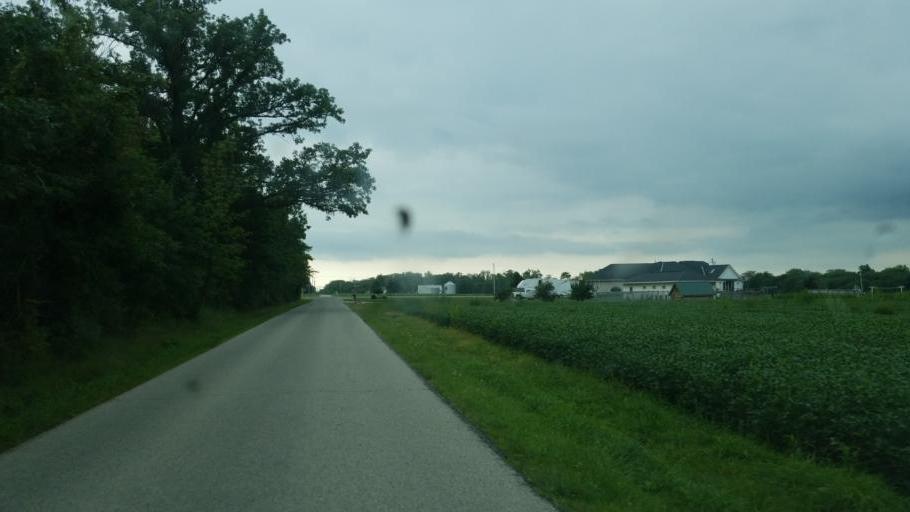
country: US
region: Ohio
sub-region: Crawford County
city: Galion
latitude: 40.7359
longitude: -82.8488
